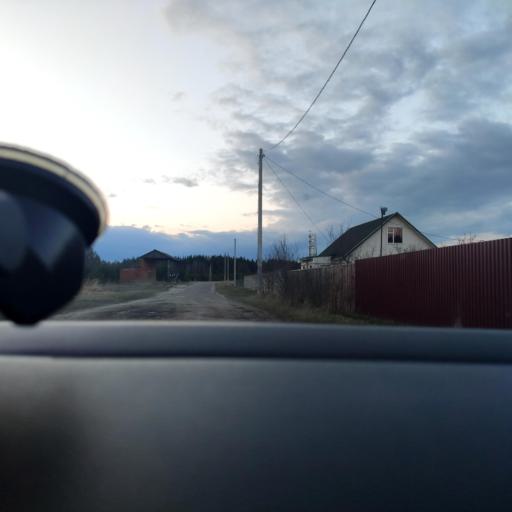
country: RU
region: Moskovskaya
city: Shaturtorf
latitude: 55.4343
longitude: 39.4274
